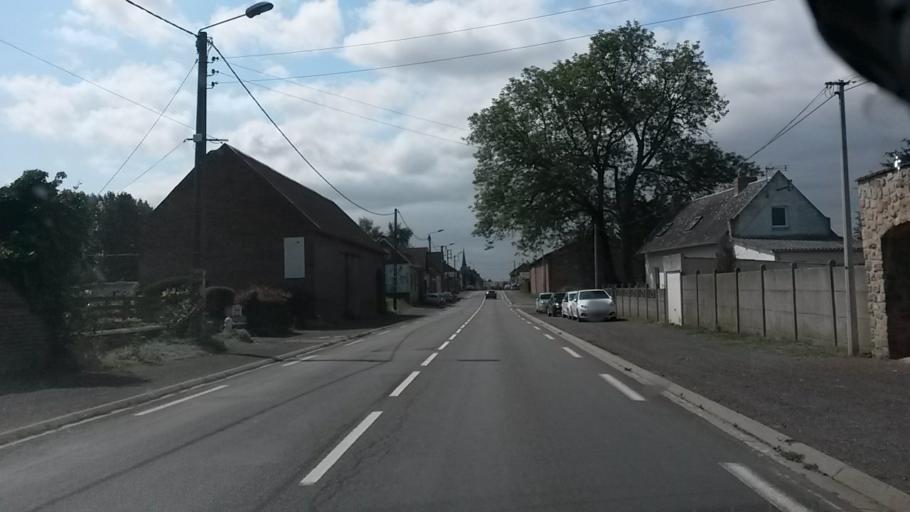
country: FR
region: Nord-Pas-de-Calais
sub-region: Departement du Pas-de-Calais
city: Vaulx-Vraucourt
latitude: 50.1208
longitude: 2.9391
